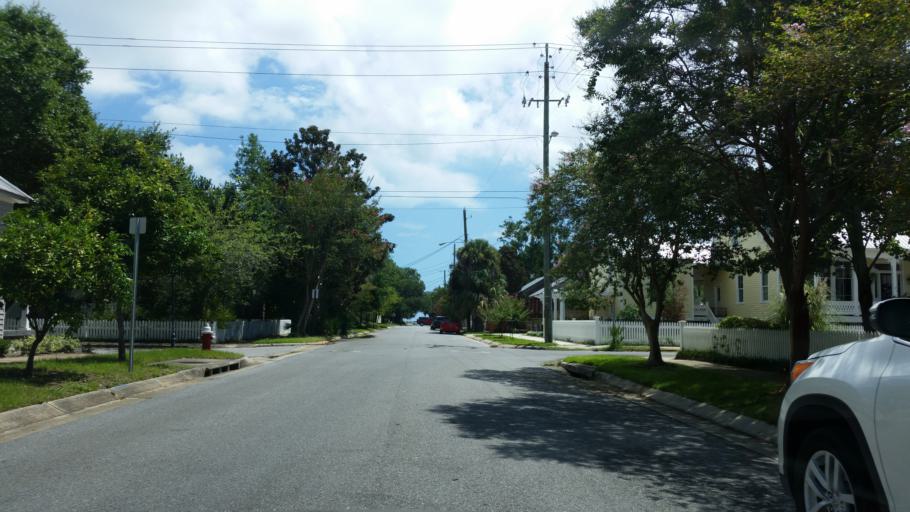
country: US
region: Florida
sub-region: Escambia County
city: Pensacola
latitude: 30.4118
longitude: -87.2080
